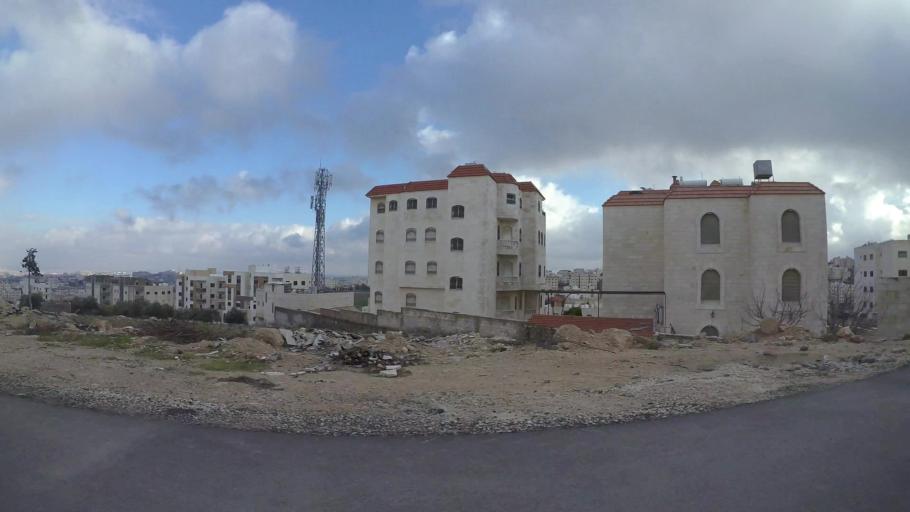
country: JO
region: Amman
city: Al Jubayhah
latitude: 32.0546
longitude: 35.8938
